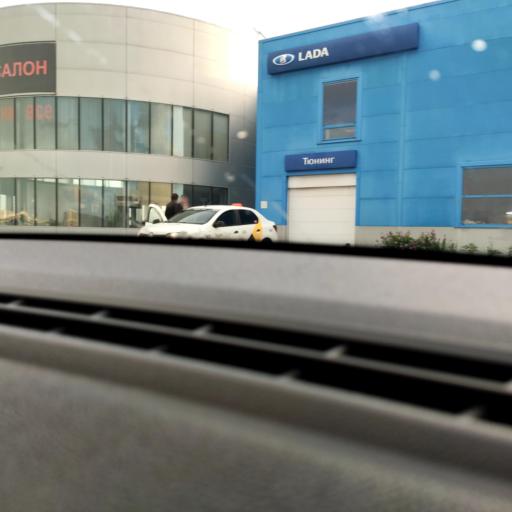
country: RU
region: Samara
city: Tol'yatti
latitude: 53.5535
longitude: 49.3396
